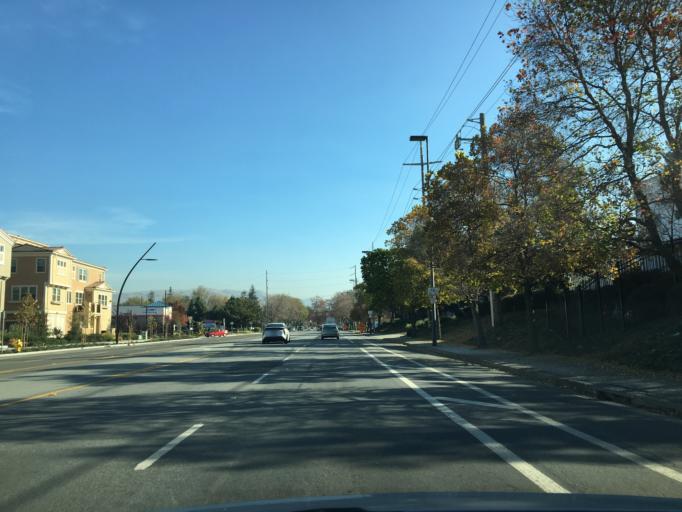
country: US
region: California
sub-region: Santa Clara County
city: Milpitas
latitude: 37.4035
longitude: -121.8938
